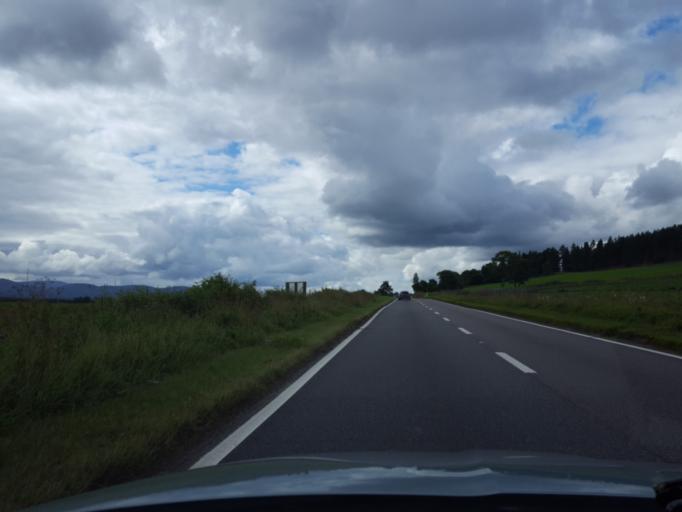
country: GB
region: Scotland
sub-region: Highland
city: Grantown on Spey
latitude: 57.3128
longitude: -3.6306
